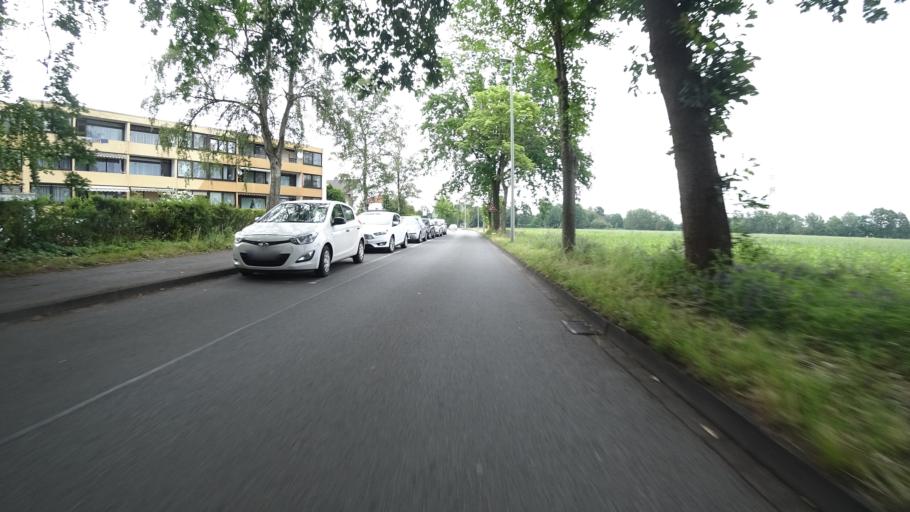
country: DE
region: North Rhine-Westphalia
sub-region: Regierungsbezirk Detmold
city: Guetersloh
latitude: 51.9320
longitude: 8.3688
